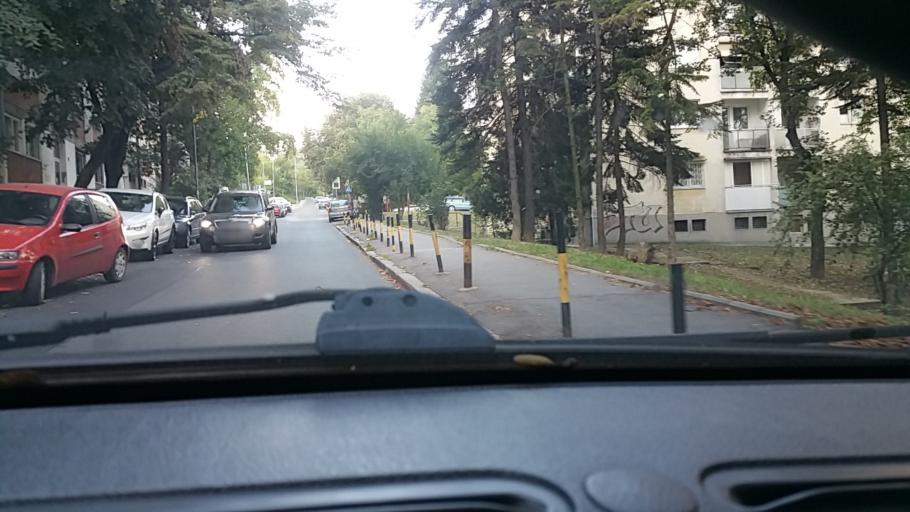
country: RS
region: Central Serbia
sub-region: Belgrade
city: Rakovica
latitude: 44.7503
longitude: 20.4590
